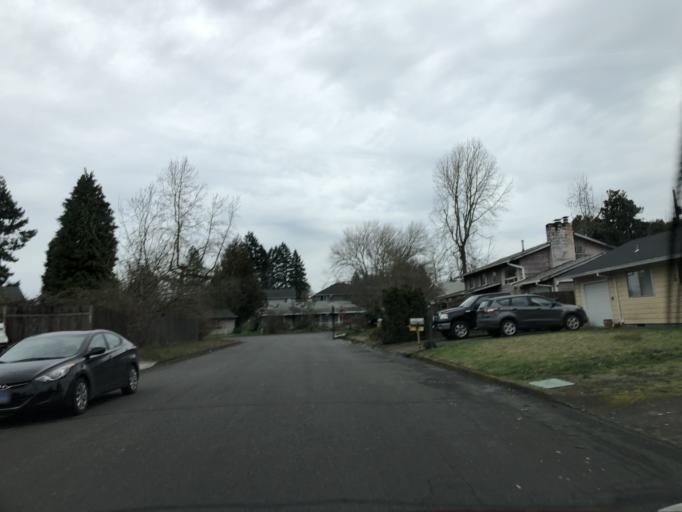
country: US
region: Oregon
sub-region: Washington County
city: Tigard
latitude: 45.4305
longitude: -122.7820
